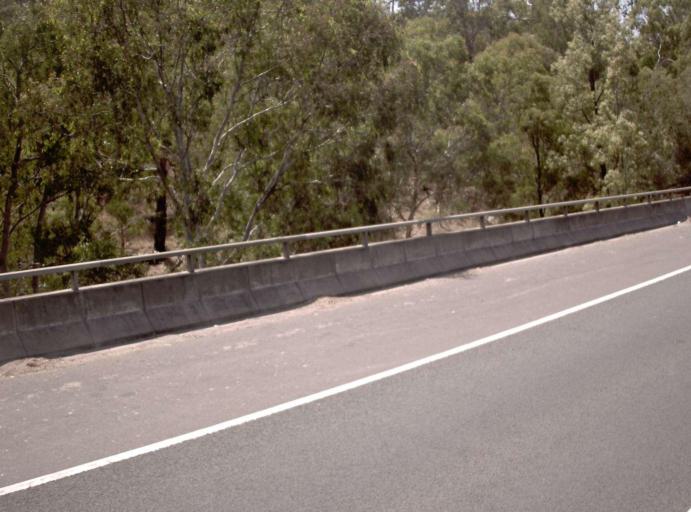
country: AU
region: Victoria
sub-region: Darebin
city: Fairfield
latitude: -37.7908
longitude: 145.0187
